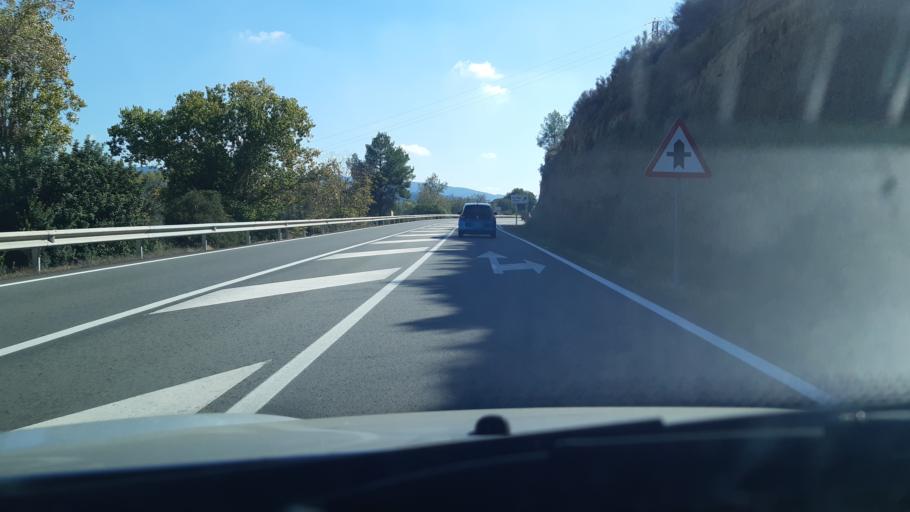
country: ES
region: Catalonia
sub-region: Provincia de Tarragona
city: Tortosa
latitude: 40.8582
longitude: 0.5112
